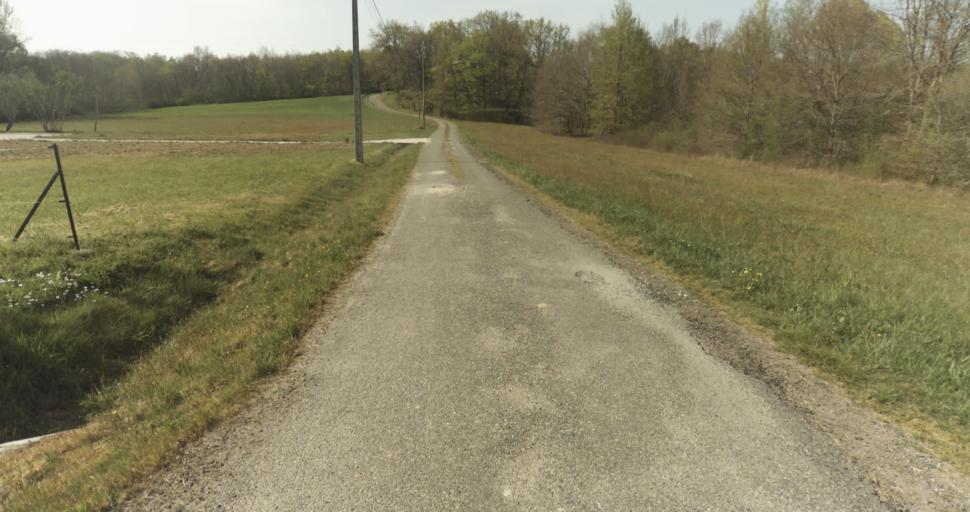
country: FR
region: Midi-Pyrenees
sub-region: Departement du Tarn-et-Garonne
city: Lafrancaise
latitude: 44.1488
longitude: 1.1808
